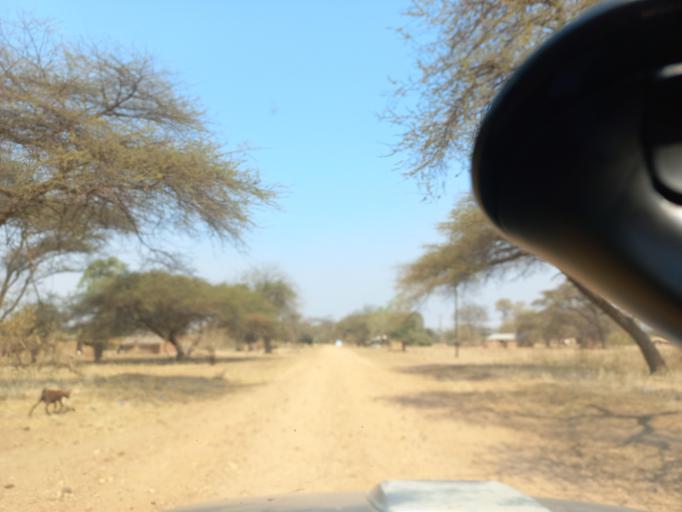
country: ZW
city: Chirundu
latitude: -15.9415
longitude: 28.8273
